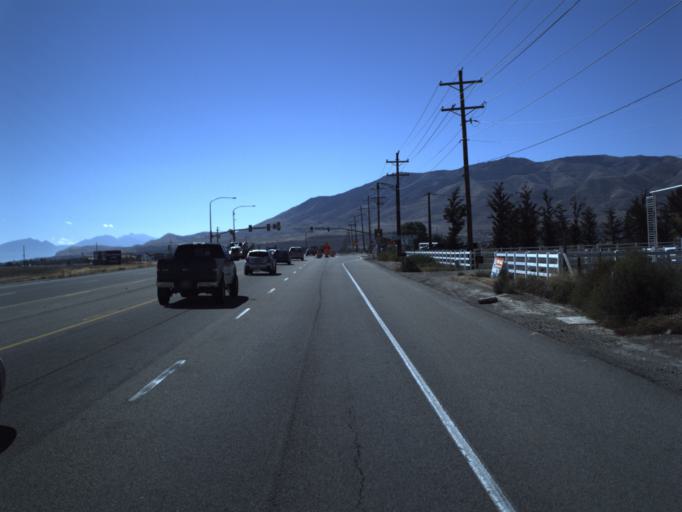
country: US
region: Utah
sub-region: Utah County
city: Saratoga Springs
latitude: 40.3639
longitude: -111.9164
